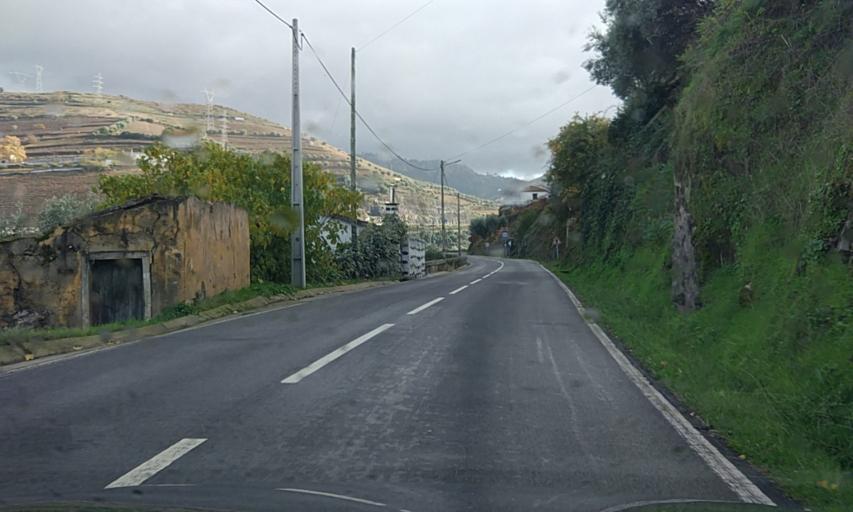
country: PT
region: Vila Real
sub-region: Peso da Regua
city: Peso da Regua
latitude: 41.1423
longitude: -7.7796
